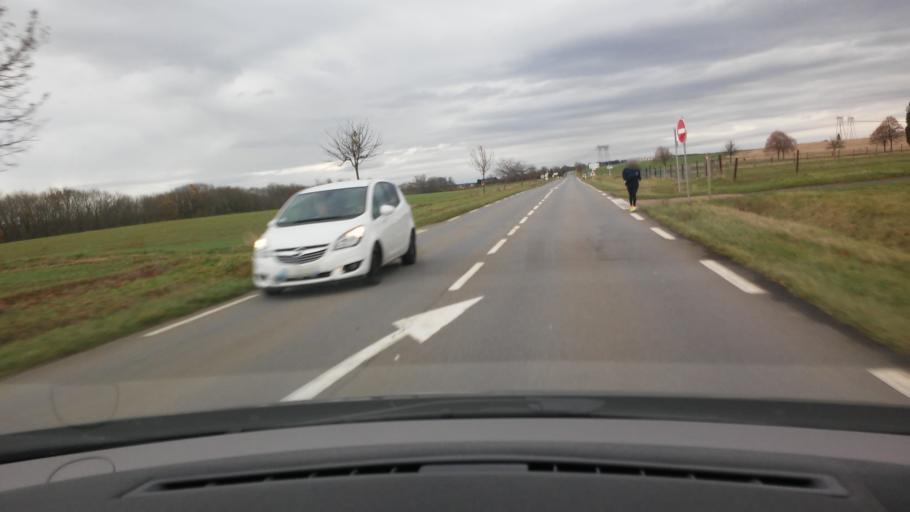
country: FR
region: Lorraine
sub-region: Departement de la Moselle
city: Retonfey
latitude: 49.1555
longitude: 6.2691
